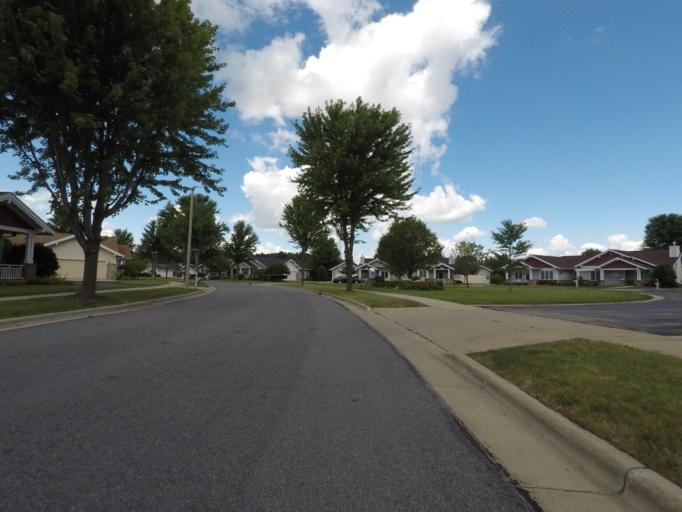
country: US
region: Wisconsin
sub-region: Dane County
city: Middleton
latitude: 43.0699
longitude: -89.5339
